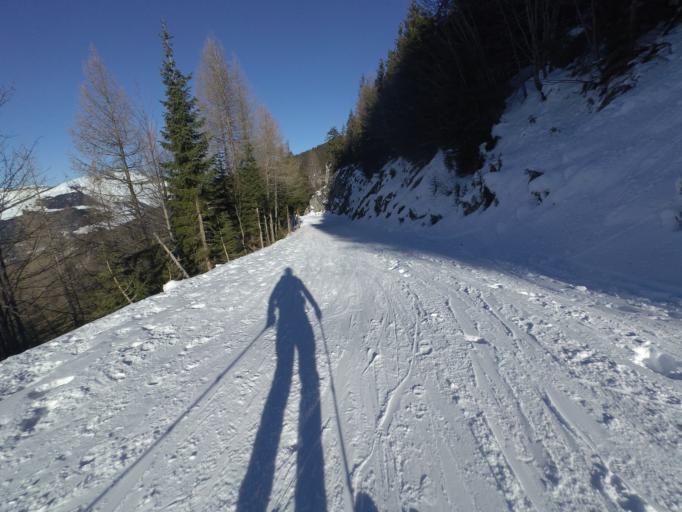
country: AT
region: Salzburg
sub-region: Politischer Bezirk Hallein
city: Scheffau am Tennengebirge
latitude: 47.6398
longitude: 13.2561
